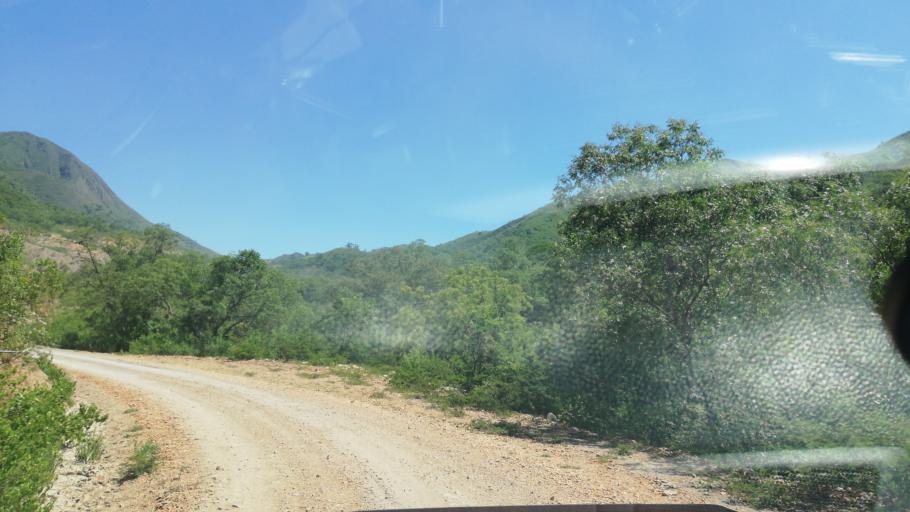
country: BO
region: Cochabamba
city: Mizque
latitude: -17.8827
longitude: -65.2861
